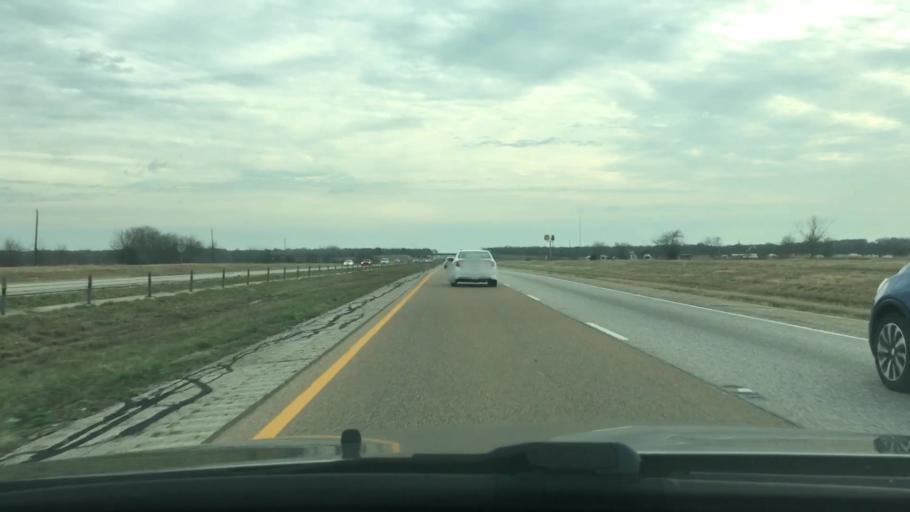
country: US
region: Texas
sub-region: Leon County
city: Centerville
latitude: 31.1008
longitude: -95.9639
